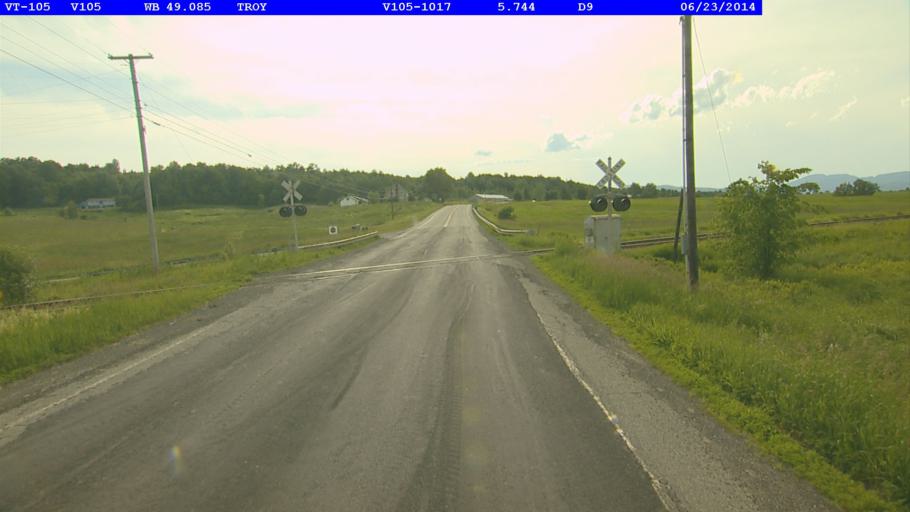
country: US
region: Vermont
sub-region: Orleans County
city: Newport
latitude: 44.9800
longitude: -72.3474
